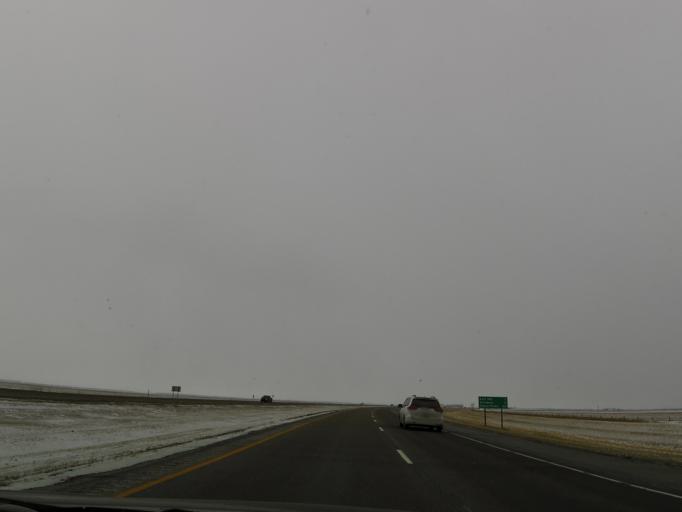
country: US
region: North Dakota
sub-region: Traill County
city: Hillsboro
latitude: 47.2491
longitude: -97.0155
